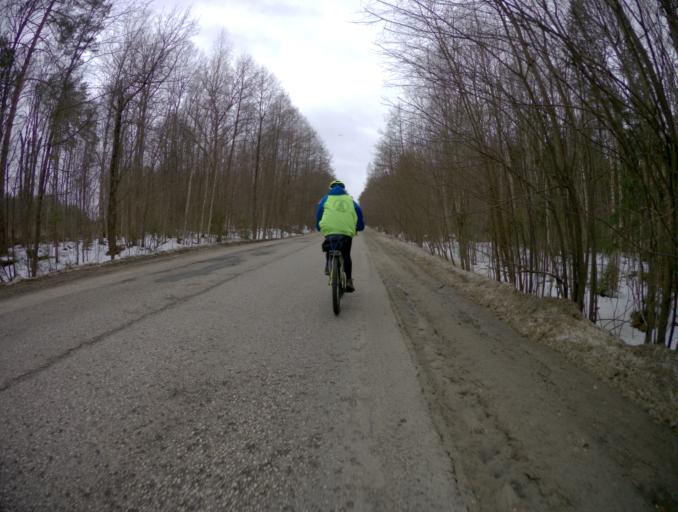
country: RU
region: Vladimir
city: Bogolyubovo
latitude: 56.1536
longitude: 40.5613
